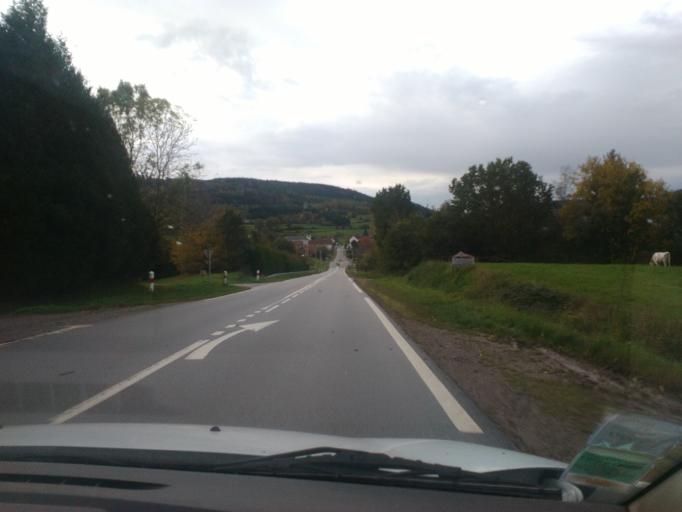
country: FR
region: Lorraine
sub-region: Departement des Vosges
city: Anould
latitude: 48.1567
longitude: 6.9215
